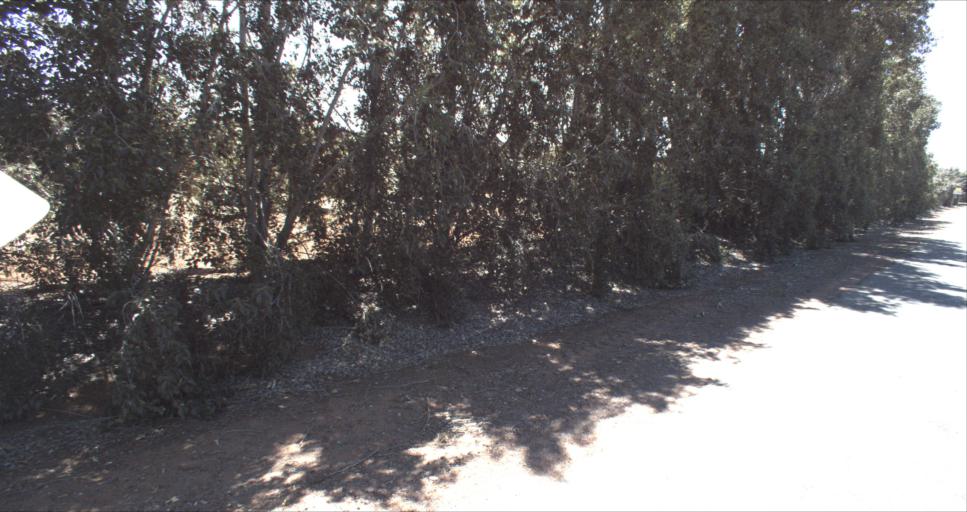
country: AU
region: New South Wales
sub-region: Leeton
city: Leeton
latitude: -34.5276
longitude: 146.3297
